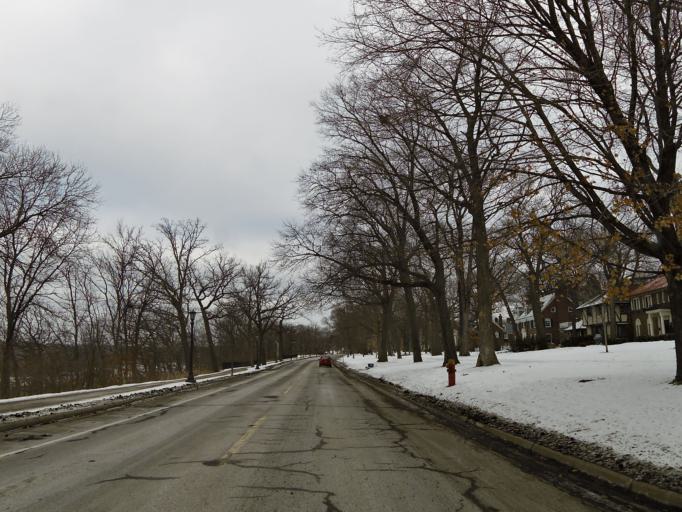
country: US
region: Minnesota
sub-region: Ramsey County
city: Lauderdale
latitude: 44.9350
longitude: -93.1985
